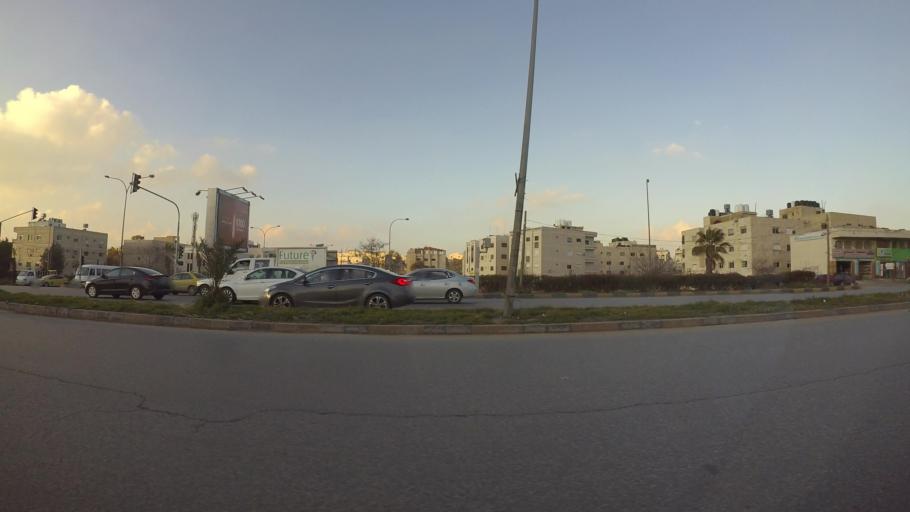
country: JO
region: Amman
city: Al Quwaysimah
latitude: 31.9123
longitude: 35.9198
